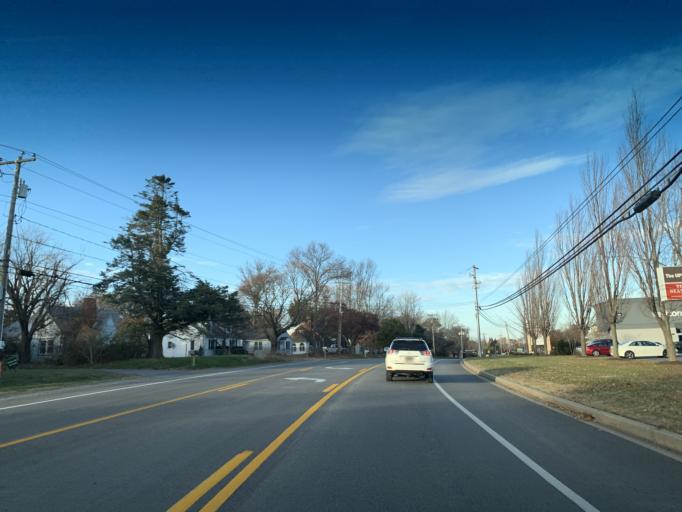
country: US
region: Maryland
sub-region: Kent County
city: Chestertown
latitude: 39.2293
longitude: -76.0727
